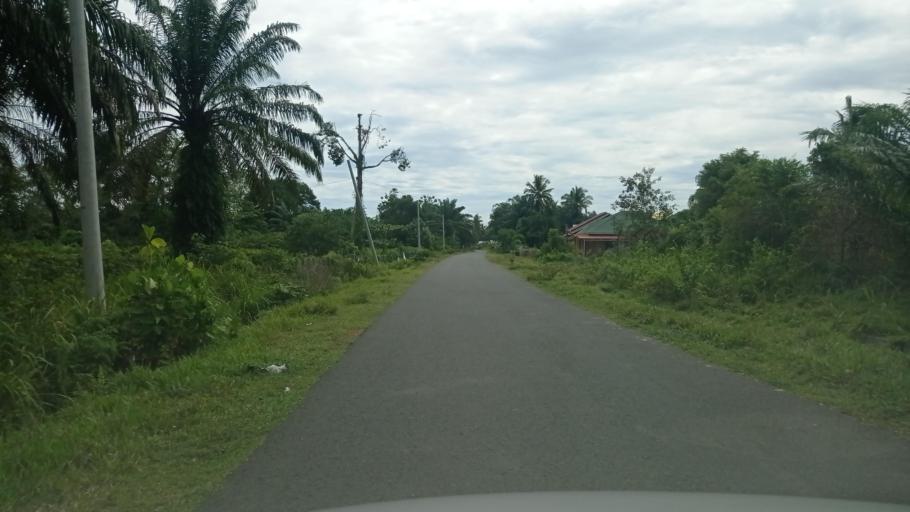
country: ID
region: Bengkulu
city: Ipuh
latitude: -2.5707
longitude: 101.1117
